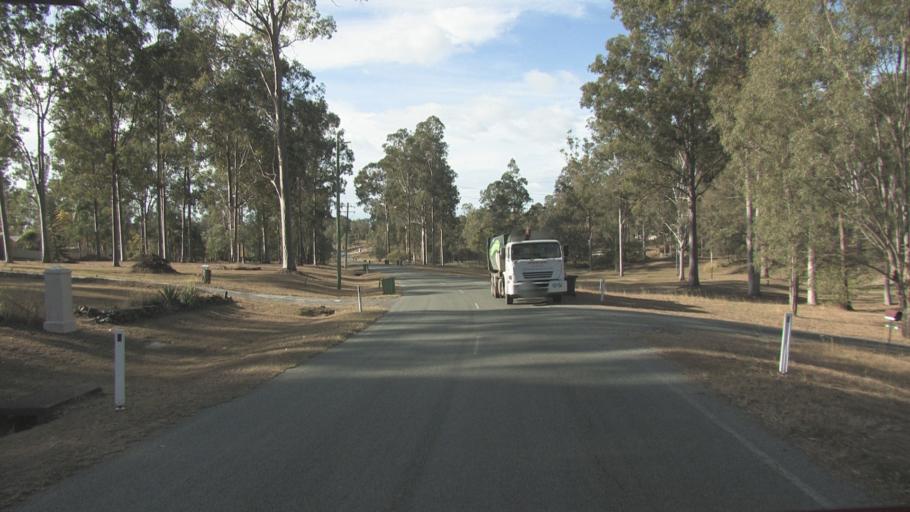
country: AU
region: Queensland
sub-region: Logan
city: Cedar Vale
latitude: -27.8798
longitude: 153.0000
